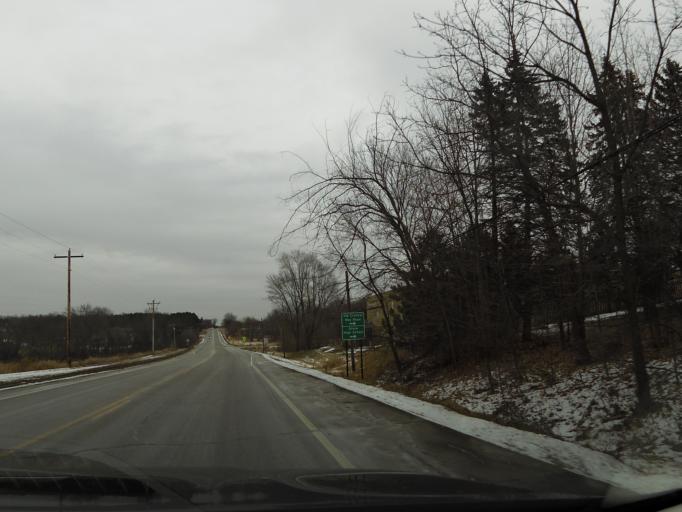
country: US
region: Minnesota
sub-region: Hennepin County
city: Long Lake
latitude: 44.9981
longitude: -93.5966
